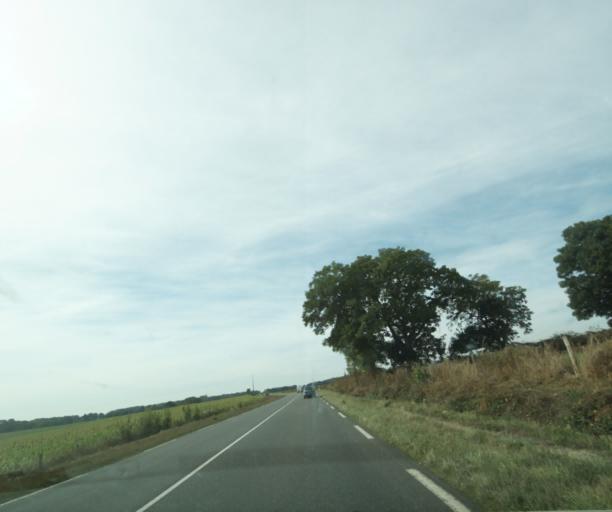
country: FR
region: Auvergne
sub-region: Departement de l'Allier
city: Lapalisse
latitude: 46.2377
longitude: 3.6050
